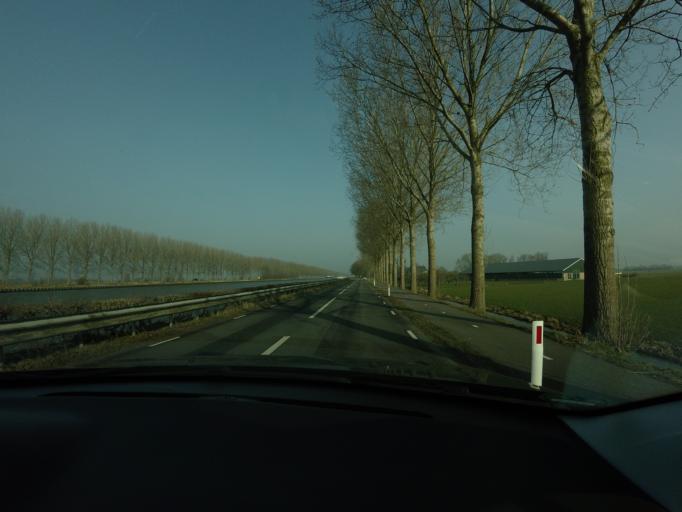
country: NL
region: Utrecht
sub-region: Stichtse Vecht
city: Vreeland
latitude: 52.2415
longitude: 5.0116
